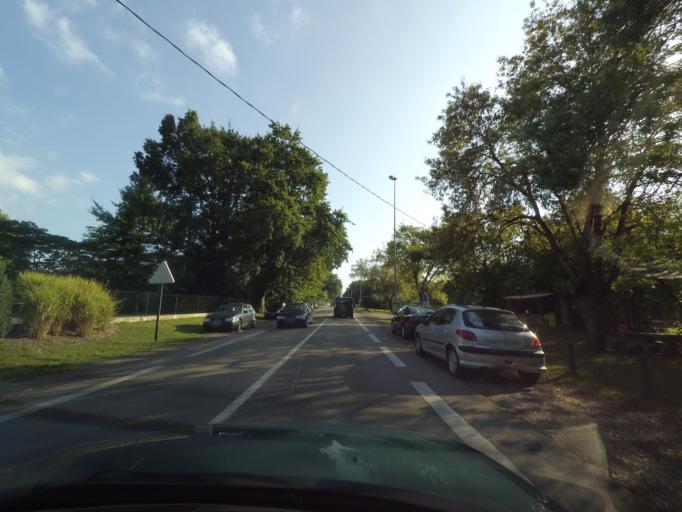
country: FR
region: Pays de la Loire
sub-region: Departement de la Loire-Atlantique
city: Saint-Philbert-de-Grand-Lieu
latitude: 47.0443
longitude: -1.6395
